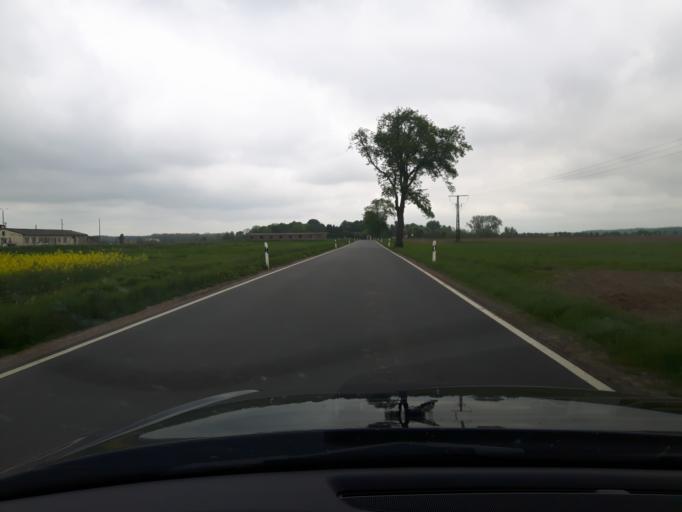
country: DE
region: Mecklenburg-Vorpommern
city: Gnoien
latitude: 54.0222
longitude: 12.6577
